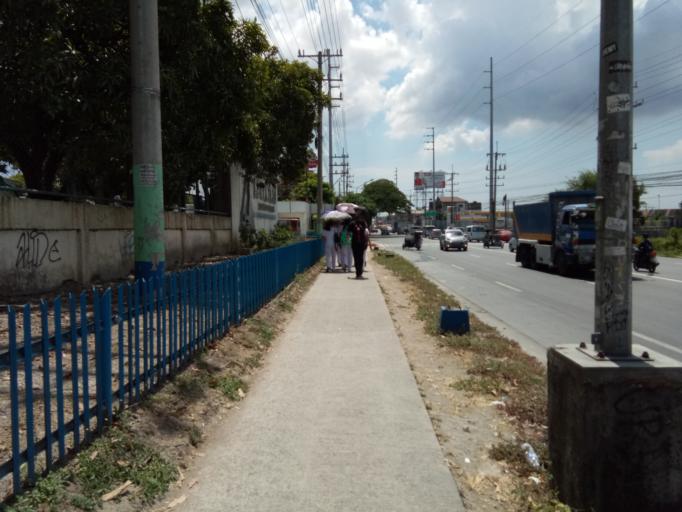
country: PH
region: Calabarzon
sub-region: Province of Cavite
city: Manggahan
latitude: 14.2920
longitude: 120.9139
